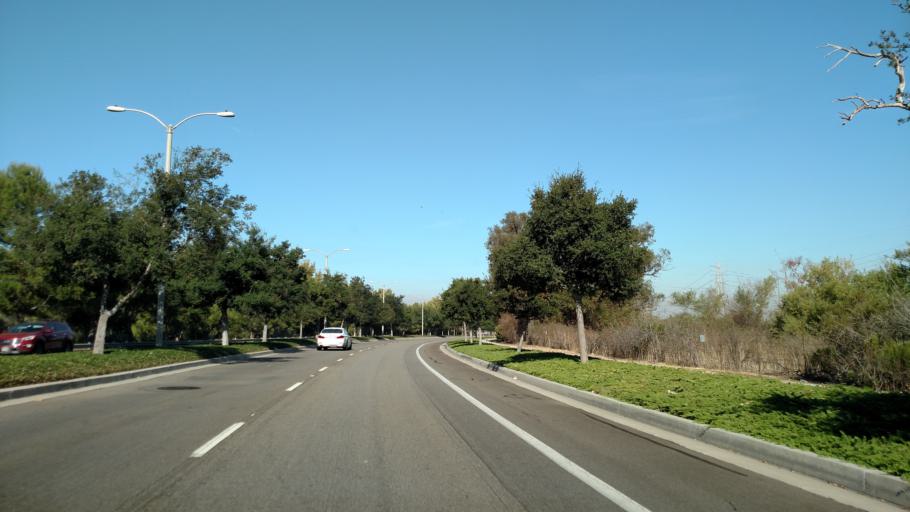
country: US
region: California
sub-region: Orange County
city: Irvine
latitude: 33.6689
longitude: -117.7778
